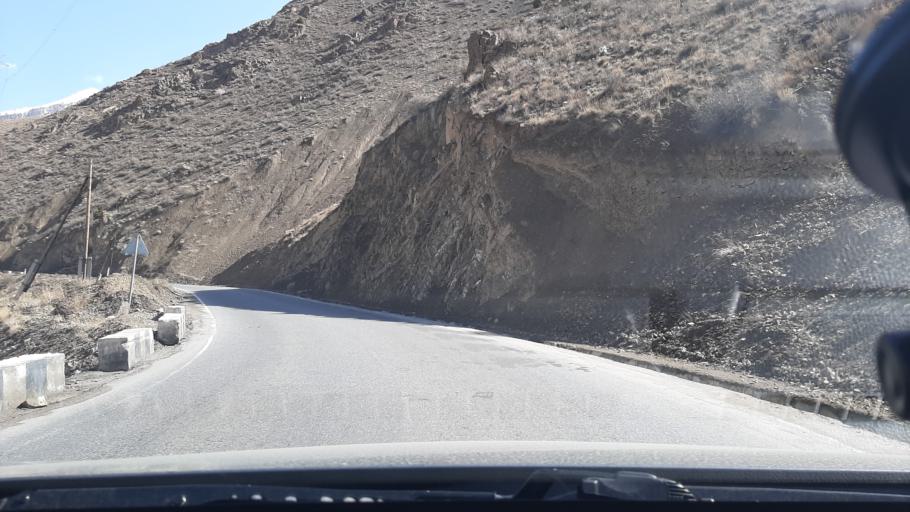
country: TJ
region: Viloyati Sughd
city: Ayni
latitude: 39.4391
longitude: 68.5488
